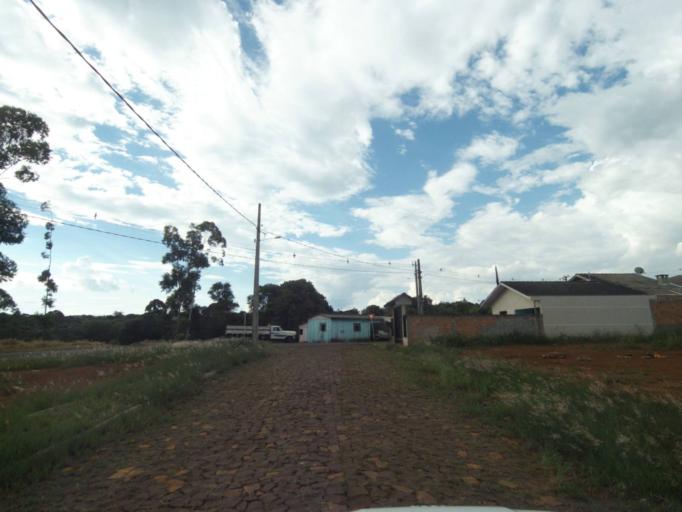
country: BR
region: Parana
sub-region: Laranjeiras Do Sul
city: Laranjeiras do Sul
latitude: -25.4961
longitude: -52.5267
